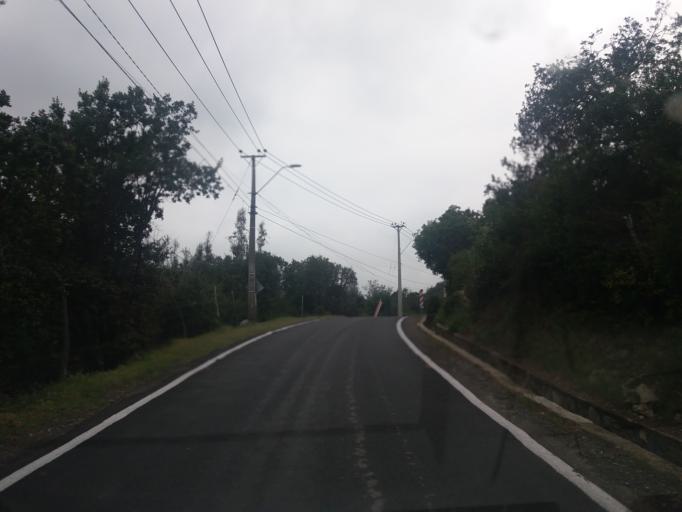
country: CL
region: Valparaiso
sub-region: Provincia de Marga Marga
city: Limache
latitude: -33.0367
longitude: -71.0918
